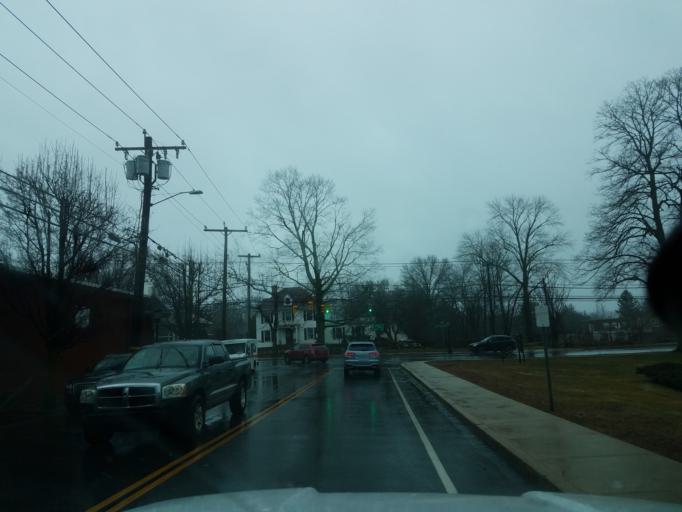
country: US
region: Connecticut
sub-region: Fairfield County
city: Darien
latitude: 41.0609
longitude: -73.4874
